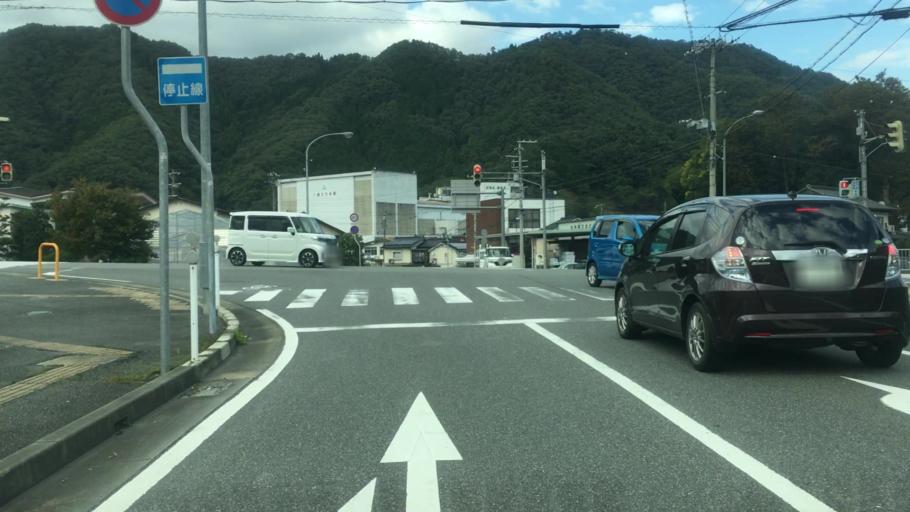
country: JP
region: Hyogo
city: Toyooka
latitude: 35.4021
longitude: 134.7676
